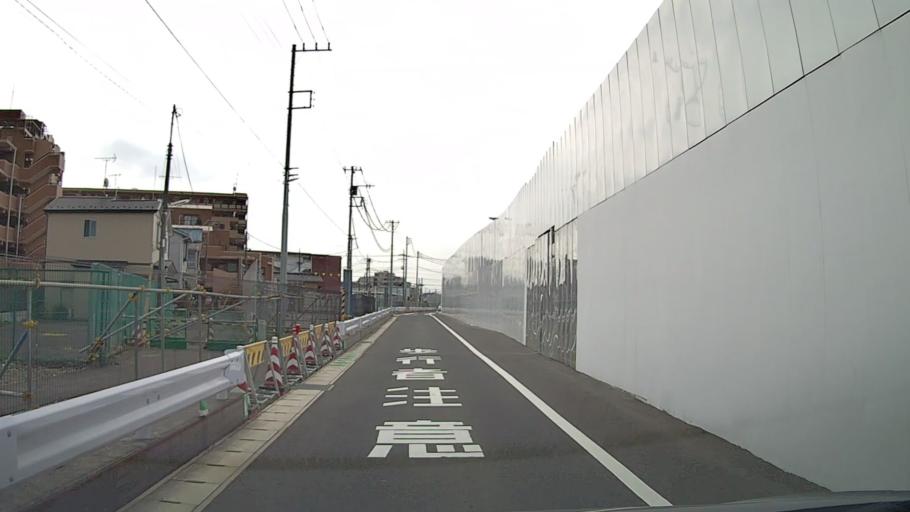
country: JP
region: Saitama
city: Wako
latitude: 35.7518
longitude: 139.5983
